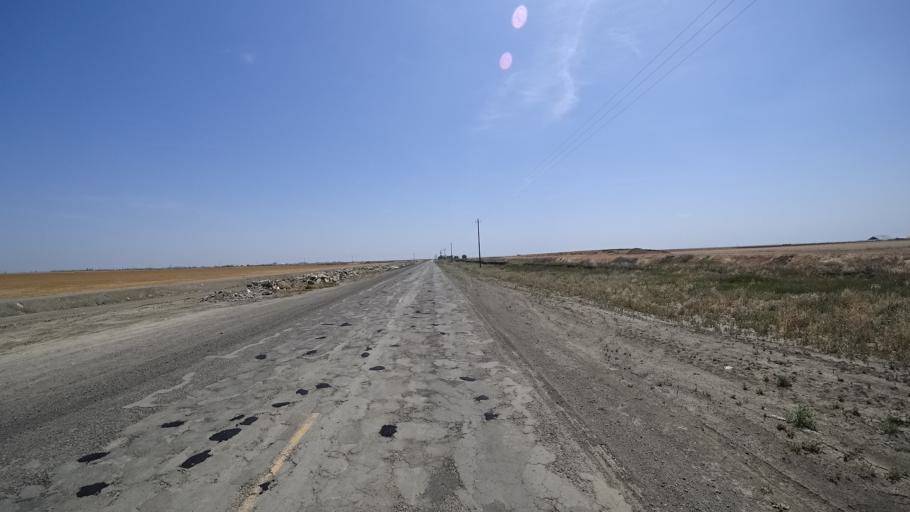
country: US
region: California
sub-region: Kings County
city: Stratford
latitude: 36.1379
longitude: -119.8921
